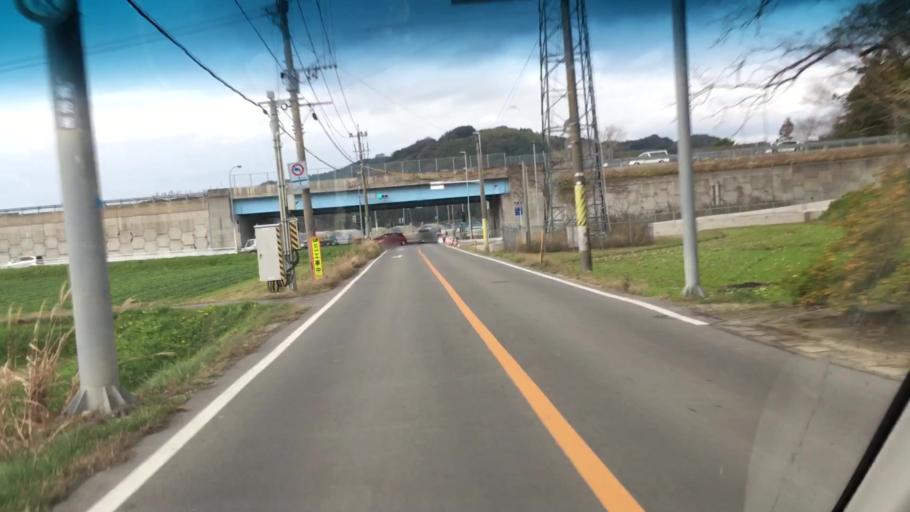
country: JP
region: Fukuoka
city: Maebaru-chuo
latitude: 33.5307
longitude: 130.1883
